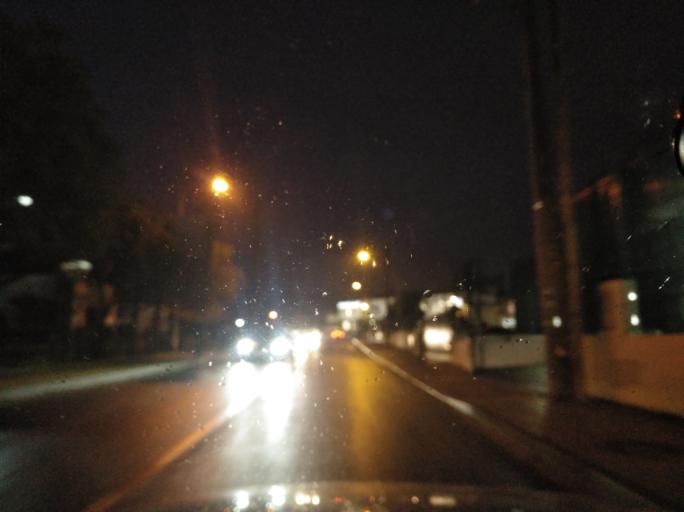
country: PT
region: Lisbon
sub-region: Loures
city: Apelacao
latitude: 38.8199
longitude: -9.1480
